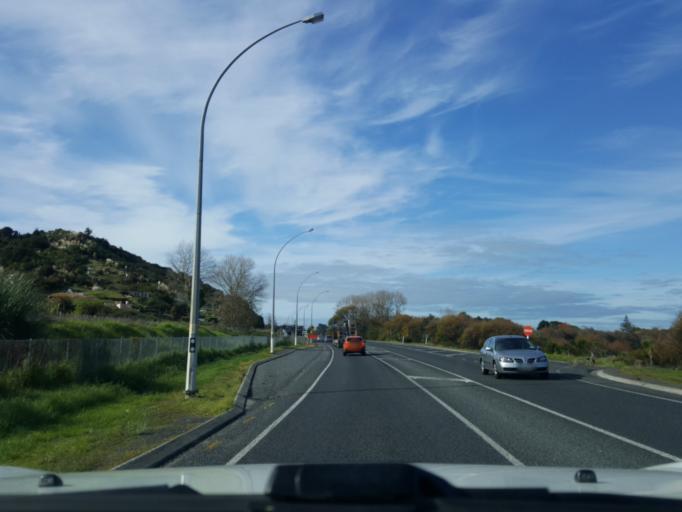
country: NZ
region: Waikato
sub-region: Waikato District
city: Ngaruawahia
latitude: -37.6075
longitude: 175.1809
